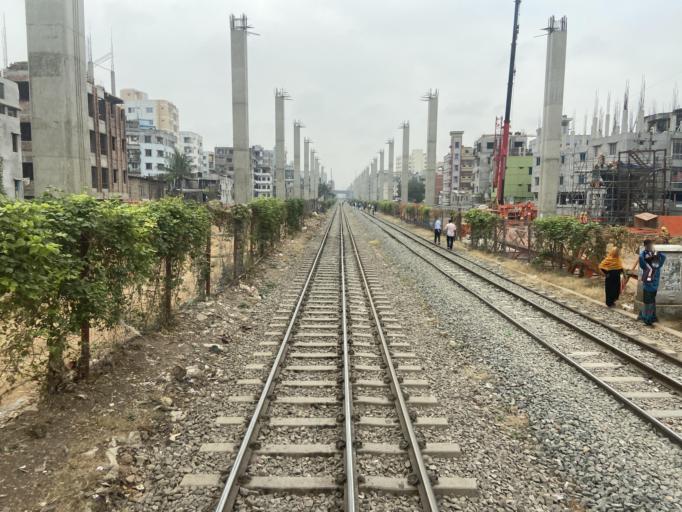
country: BD
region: Dhaka
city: Paltan
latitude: 23.7721
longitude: 90.3968
